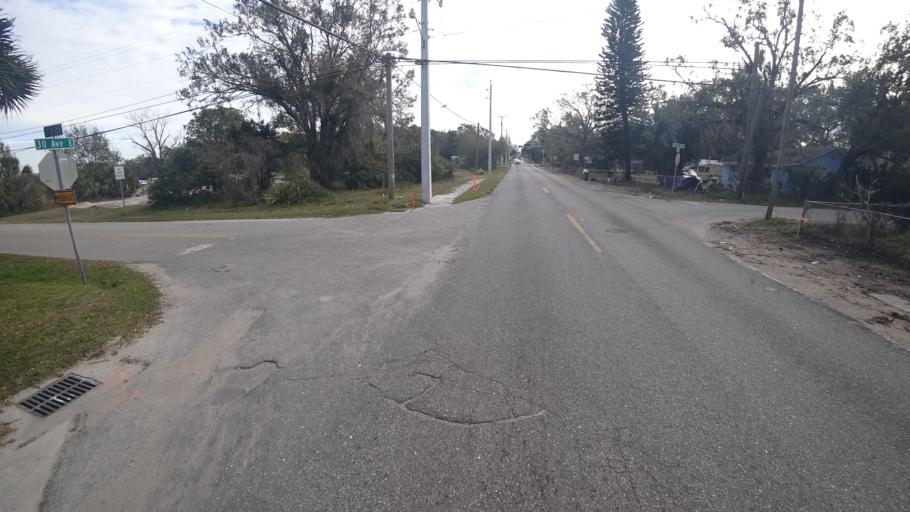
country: US
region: Florida
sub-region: Manatee County
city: West Samoset
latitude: 27.4734
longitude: -82.5503
